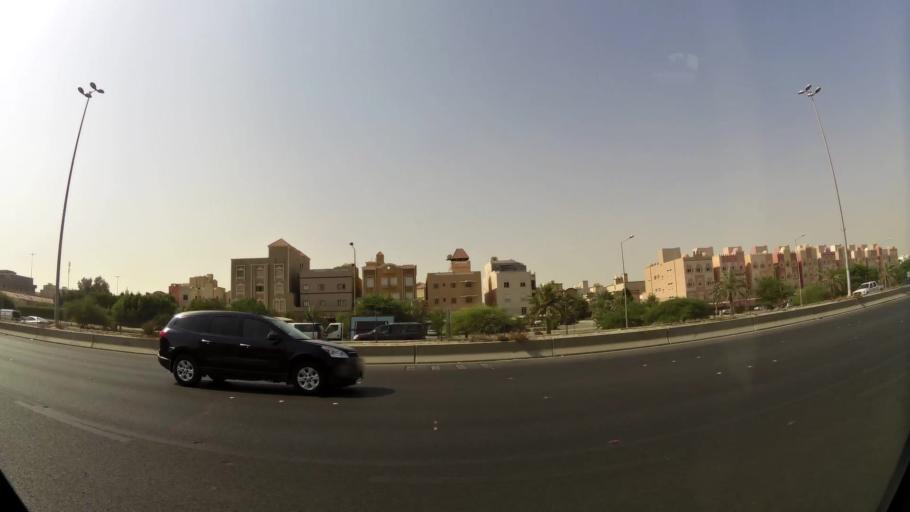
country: KW
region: Al Ahmadi
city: Al Fintas
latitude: 29.1806
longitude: 48.1134
